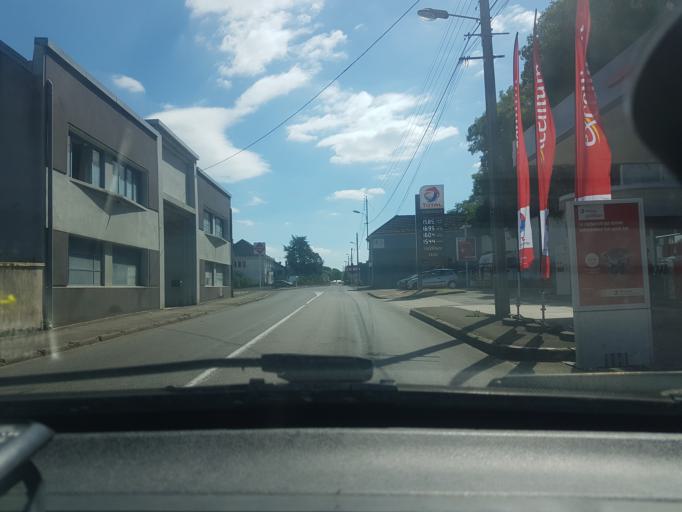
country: FR
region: Franche-Comte
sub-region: Departement de la Haute-Saone
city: Gray
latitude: 47.4448
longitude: 5.5980
